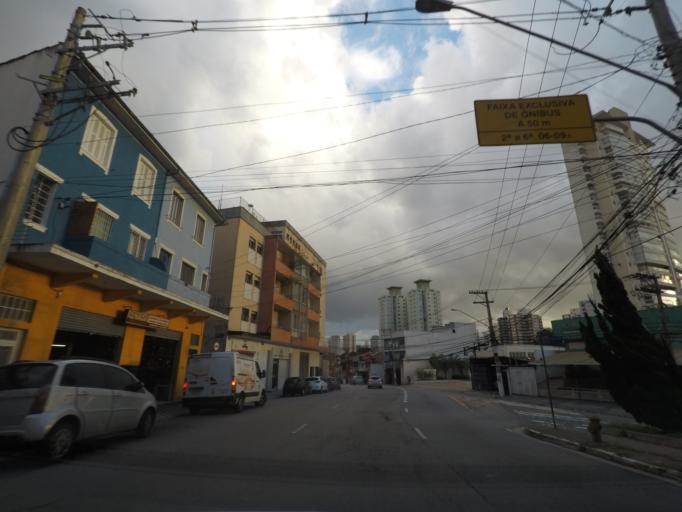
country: BR
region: Sao Paulo
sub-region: Sao Paulo
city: Sao Paulo
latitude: -23.4872
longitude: -46.6237
